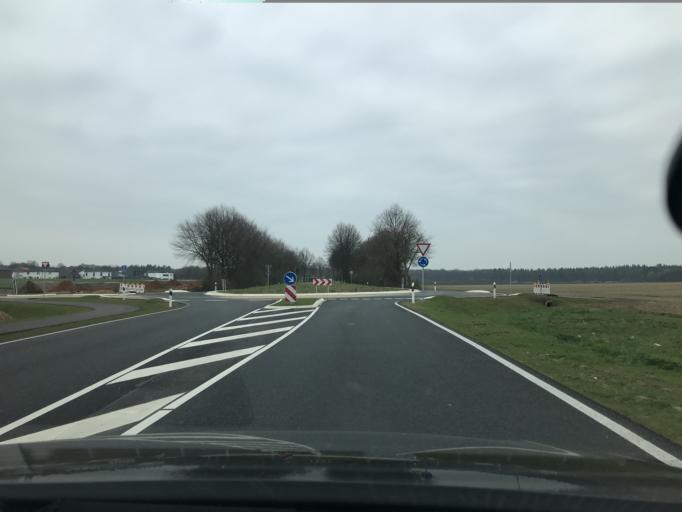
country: DE
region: North Rhine-Westphalia
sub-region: Regierungsbezirk Dusseldorf
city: Schwalmtal
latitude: 51.2118
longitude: 6.2622
